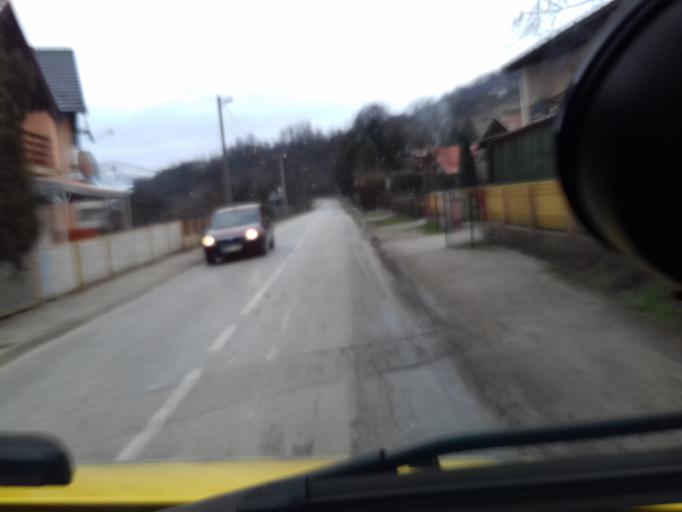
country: BA
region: Federation of Bosnia and Herzegovina
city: Zenica
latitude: 44.1865
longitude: 17.9461
